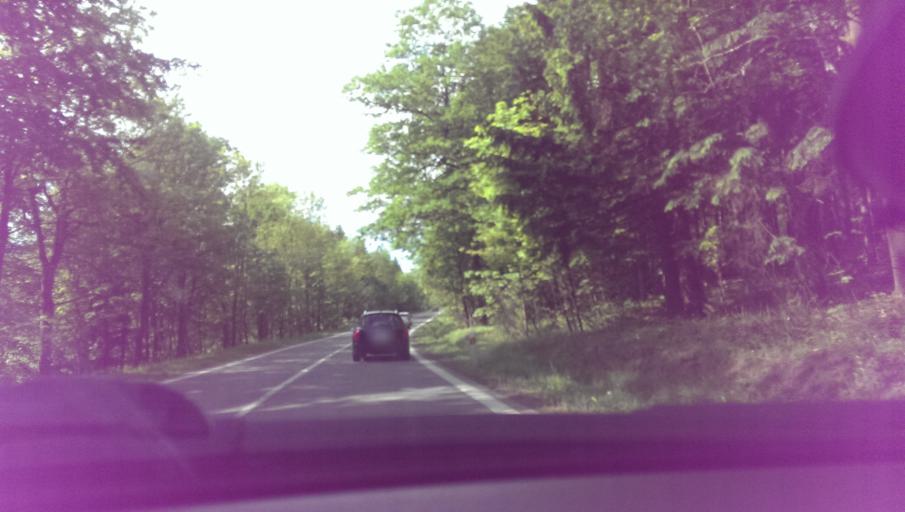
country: CZ
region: Moravskoslezsky
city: Frenstat pod Radhostem
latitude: 49.5052
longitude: 18.1907
